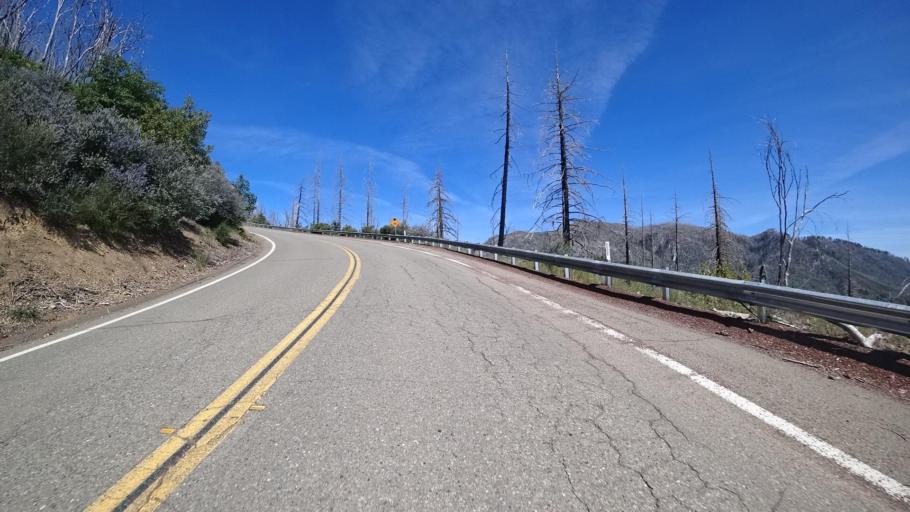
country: US
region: California
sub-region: Lake County
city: Cobb
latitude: 38.7752
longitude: -122.7281
